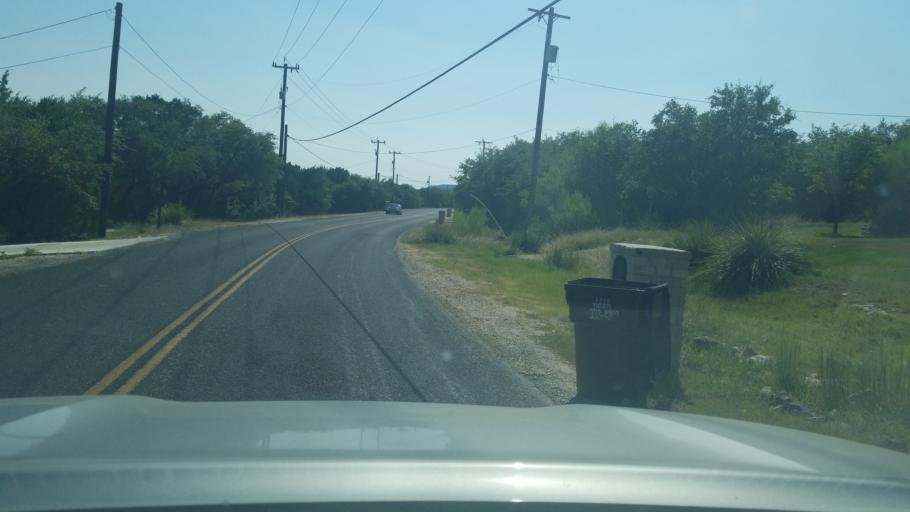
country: US
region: Texas
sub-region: Bexar County
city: Timberwood Park
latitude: 29.6772
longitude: -98.5176
